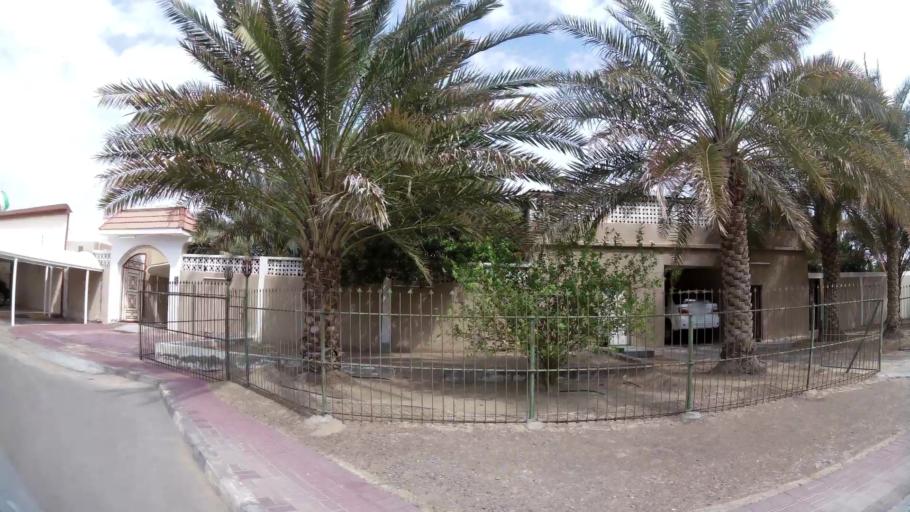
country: AE
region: Abu Dhabi
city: Al Ain
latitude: 24.1971
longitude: 55.7964
